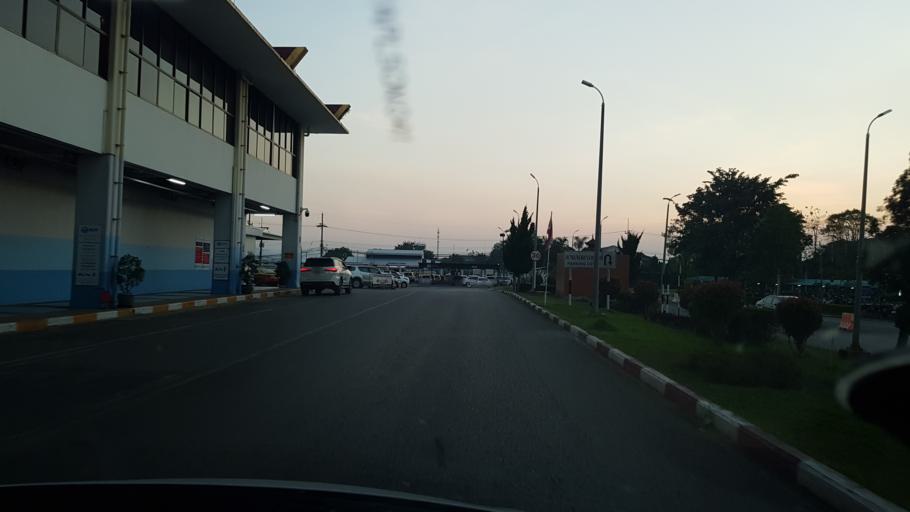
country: TH
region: Chiang Rai
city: Chiang Rai
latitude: 19.9548
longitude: 99.8789
